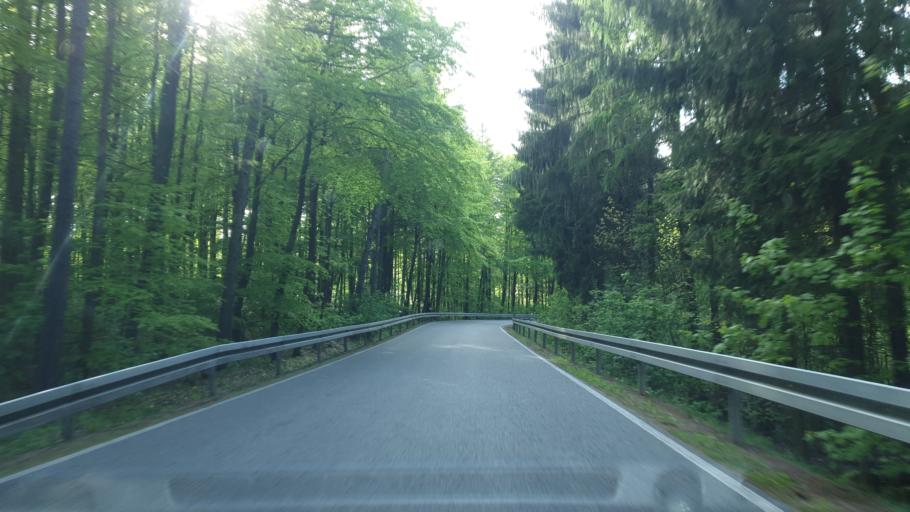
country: DE
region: Saxony
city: Hohndorf
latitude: 50.7183
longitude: 12.6530
